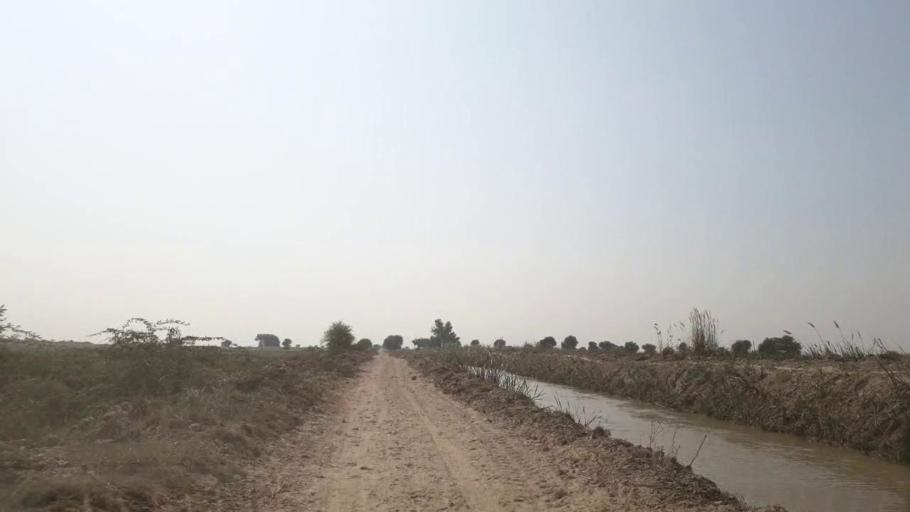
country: PK
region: Sindh
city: Bulri
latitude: 24.9777
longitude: 68.4025
